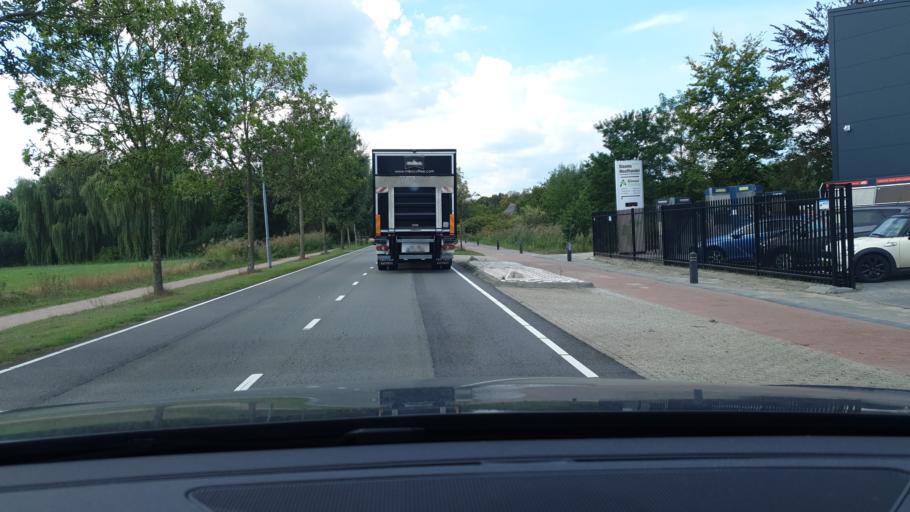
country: NL
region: North Brabant
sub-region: Gemeente Valkenswaard
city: Valkenswaard
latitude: 51.3506
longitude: 5.4408
